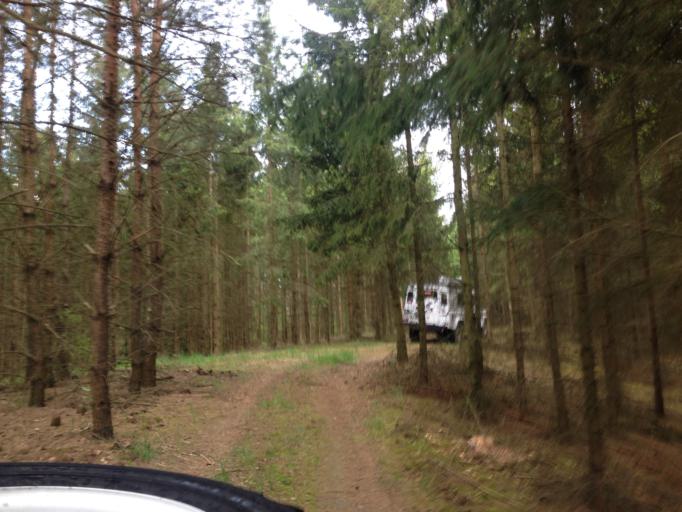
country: PL
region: Kujawsko-Pomorskie
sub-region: Powiat brodnicki
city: Bartniczka
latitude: 53.2808
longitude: 19.6583
